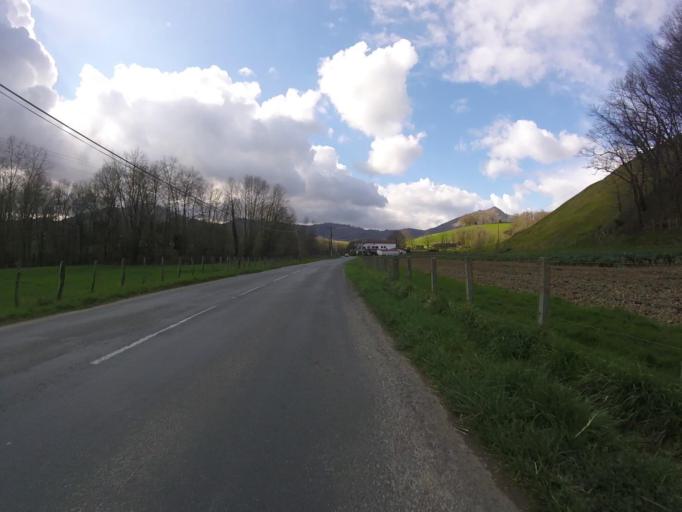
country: FR
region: Aquitaine
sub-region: Departement des Pyrenees-Atlantiques
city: Sare
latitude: 43.2927
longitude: -1.5783
